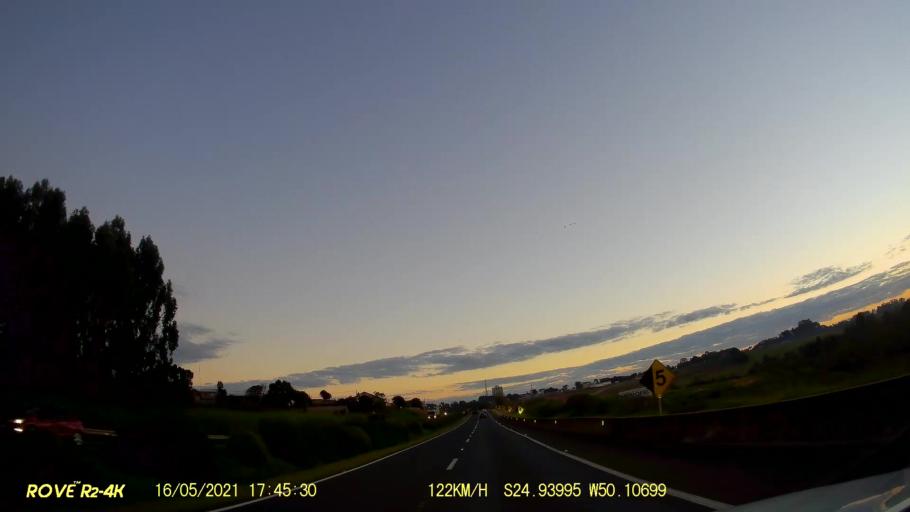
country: BR
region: Parana
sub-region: Carambei
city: Carambei
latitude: -24.9394
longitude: -50.1063
